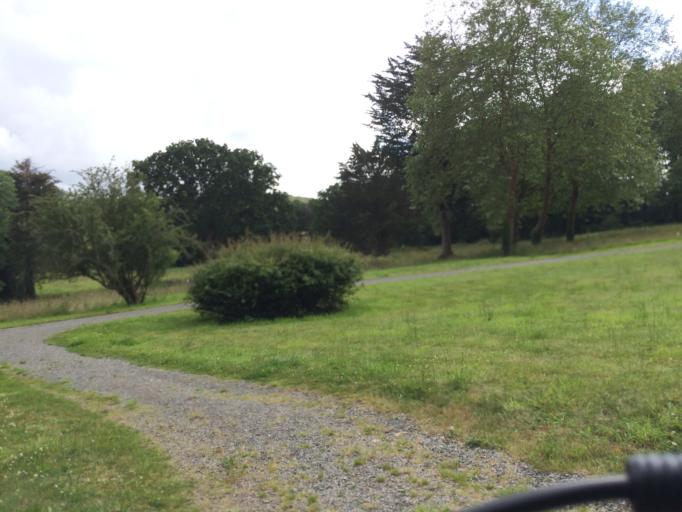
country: FR
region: Brittany
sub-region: Departement du Finistere
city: Logonna-Daoulas
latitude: 48.3220
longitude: -4.2721
